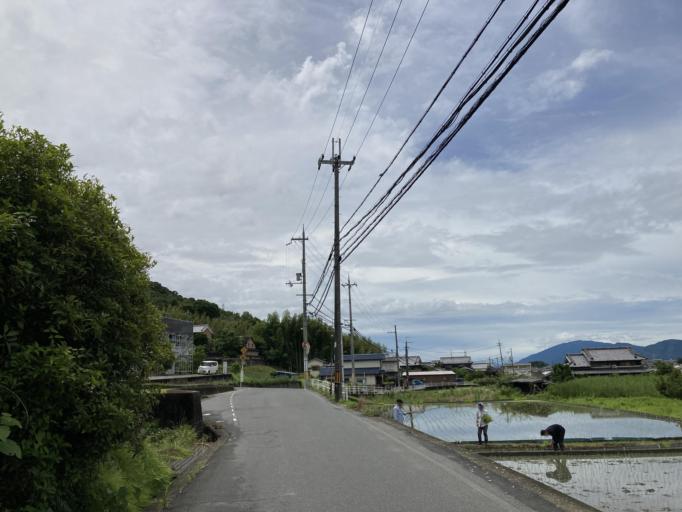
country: JP
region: Nara
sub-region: Ikoma-shi
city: Ikoma
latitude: 34.6220
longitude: 135.7087
